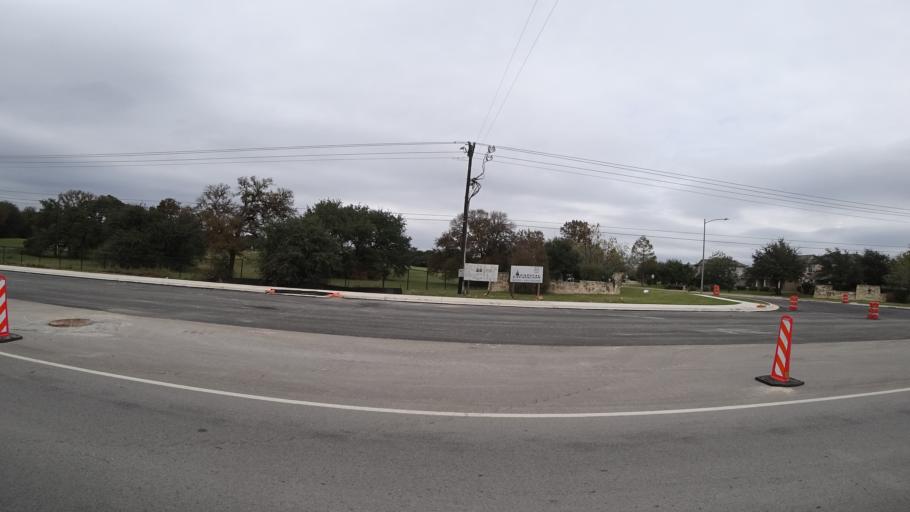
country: US
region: Texas
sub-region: Travis County
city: Manchaca
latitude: 30.1495
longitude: -97.8438
